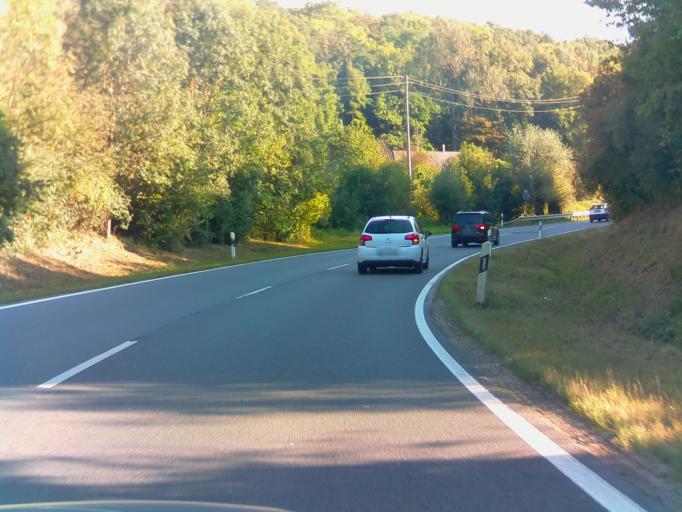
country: DE
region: Bavaria
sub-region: Regierungsbezirk Unterfranken
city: Gaukonigshofen
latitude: 49.6533
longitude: 10.0283
